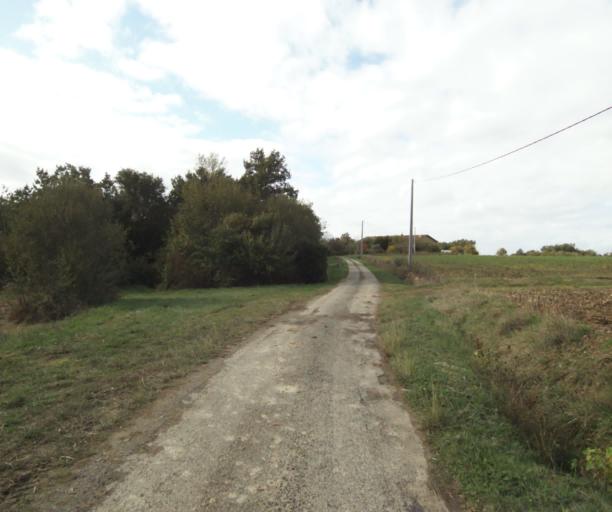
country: FR
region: Midi-Pyrenees
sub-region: Departement du Tarn-et-Garonne
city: Finhan
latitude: 43.9075
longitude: 1.1446
